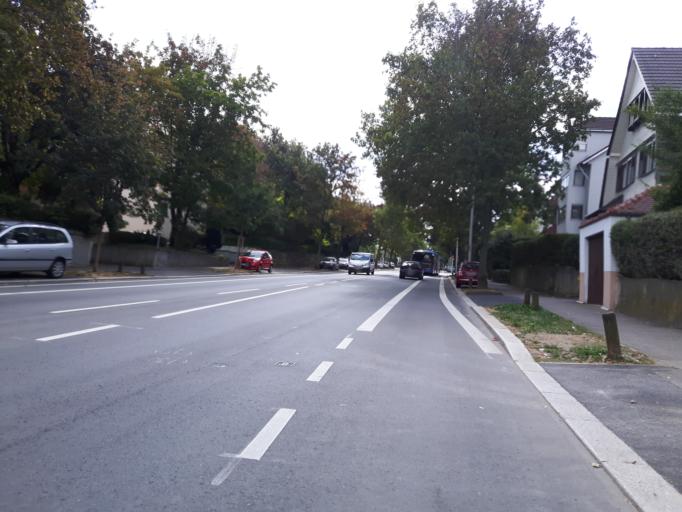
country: DE
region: Baden-Wuerttemberg
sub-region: Regierungsbezirk Stuttgart
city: Heilbronn
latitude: 49.1300
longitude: 9.2176
